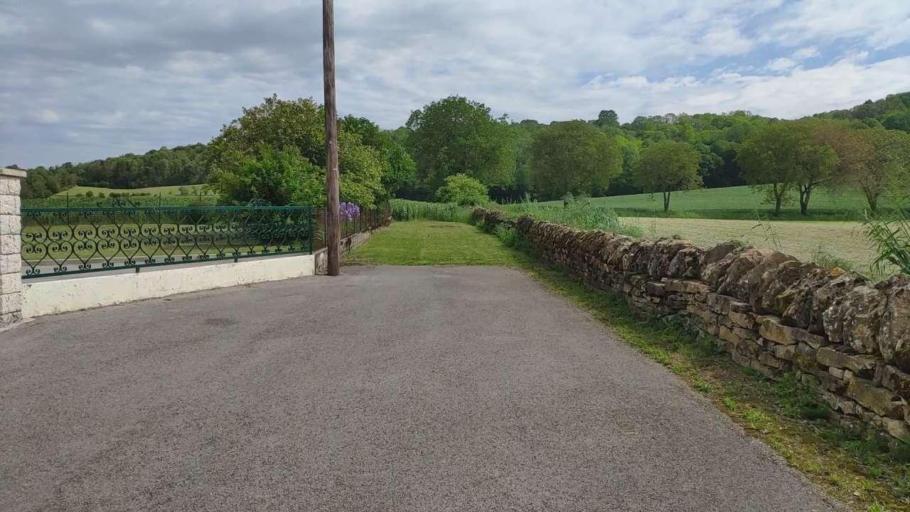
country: FR
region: Franche-Comte
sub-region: Departement du Jura
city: Poligny
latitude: 46.7704
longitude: 5.6197
